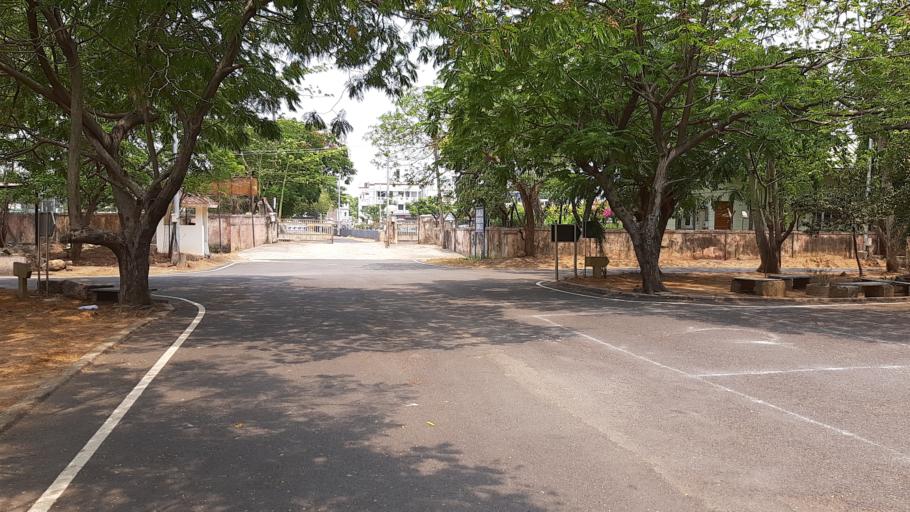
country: IN
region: Tamil Nadu
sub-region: Kancheepuram
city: Saint Thomas Mount
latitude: 13.0143
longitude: 80.1953
